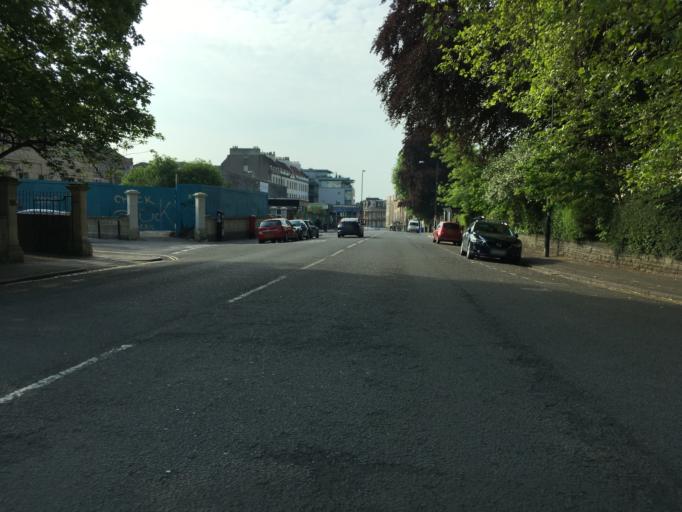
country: GB
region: England
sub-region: Bristol
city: Bristol
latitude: 51.4561
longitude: -2.6197
